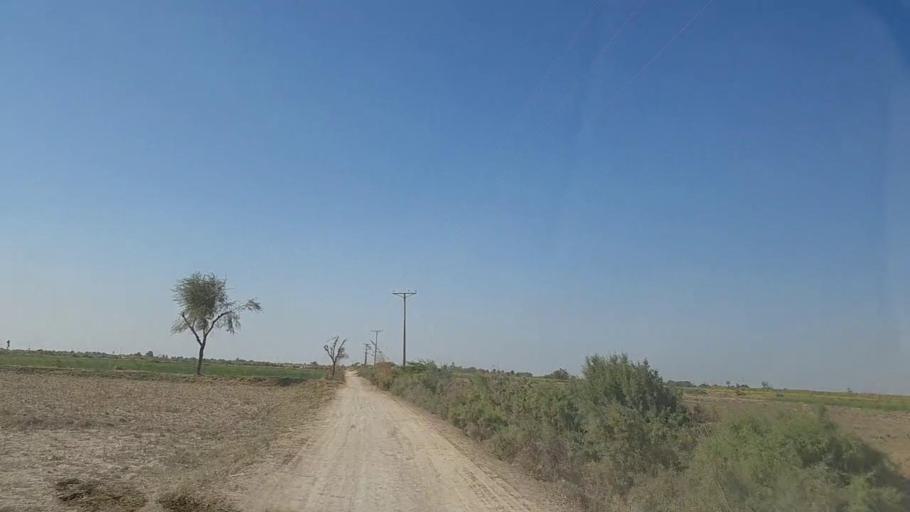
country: PK
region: Sindh
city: Digri
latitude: 25.1267
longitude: 69.0644
